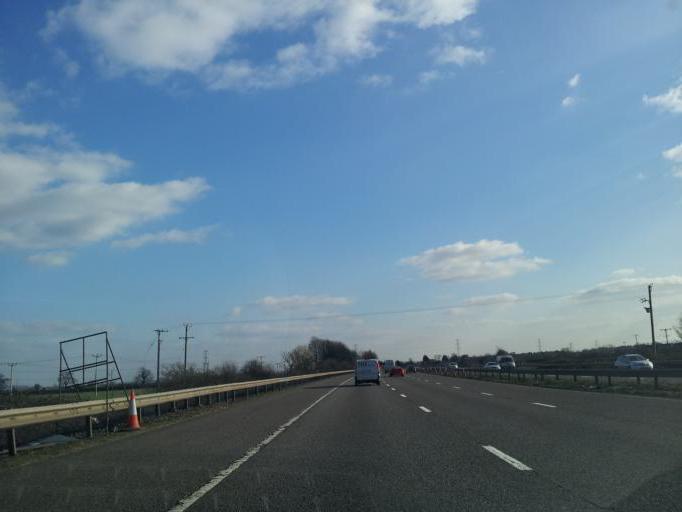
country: GB
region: England
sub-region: Somerset
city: Puriton
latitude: 51.1370
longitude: -2.9688
